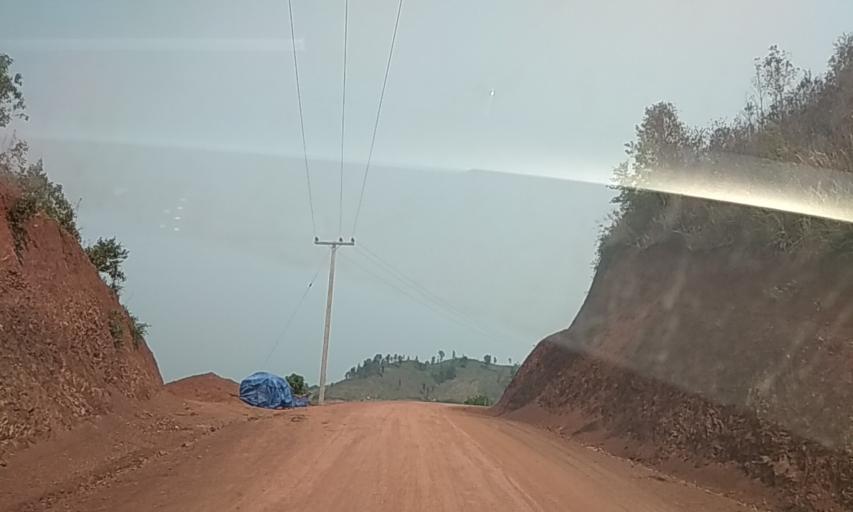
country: VN
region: Huyen Dien Bien
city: Dien Bien Phu
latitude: 21.4769
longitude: 102.7773
